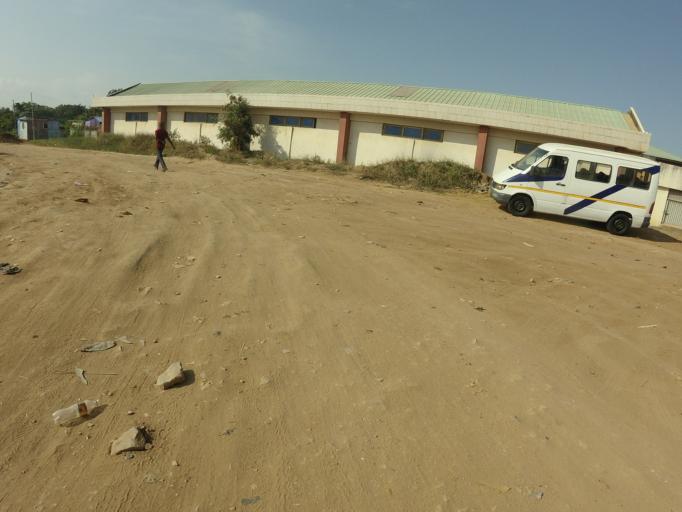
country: GH
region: Greater Accra
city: Dome
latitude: 5.6547
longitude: -0.2654
